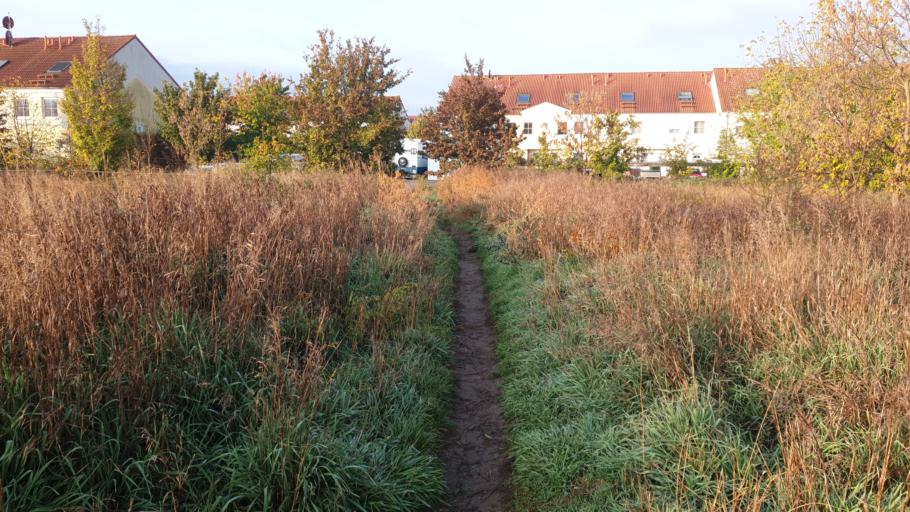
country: DE
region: Berlin
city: Gropiusstadt
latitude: 52.4020
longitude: 13.4436
